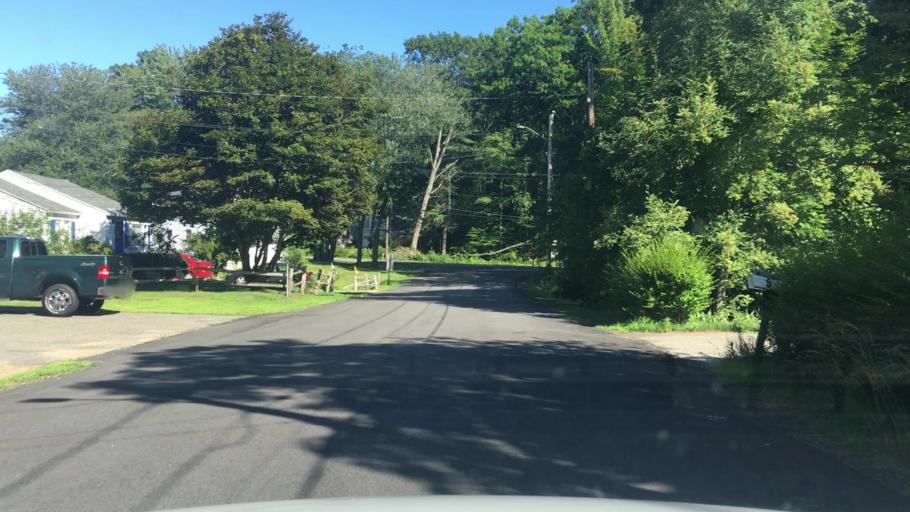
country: US
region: New Hampshire
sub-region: Rockingham County
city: Newmarket
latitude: 43.0380
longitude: -70.9509
